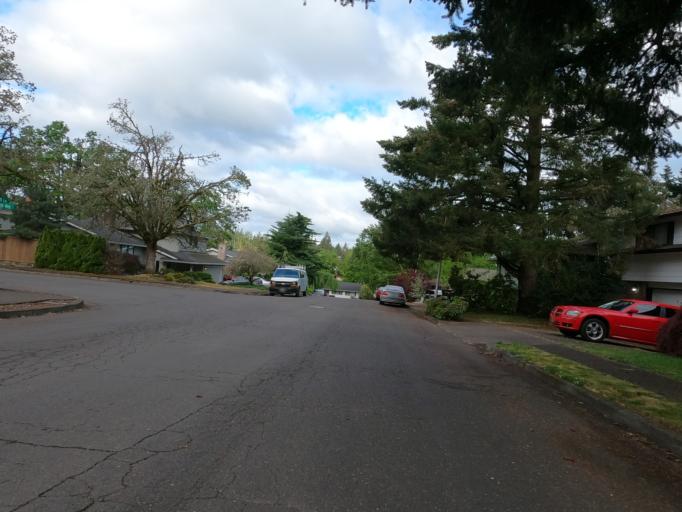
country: US
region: Oregon
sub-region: Clackamas County
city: Clackamas
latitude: 45.3979
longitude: -122.5830
